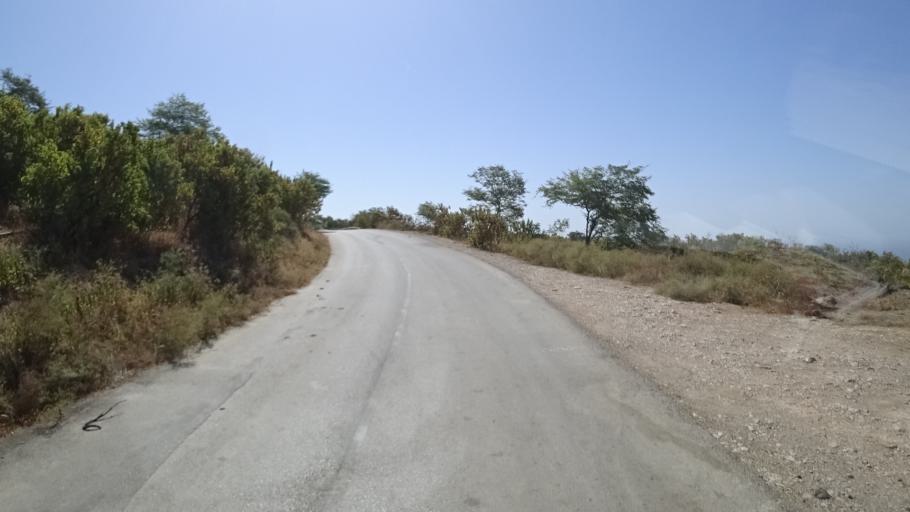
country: OM
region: Zufar
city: Salalah
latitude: 17.0736
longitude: 54.4406
